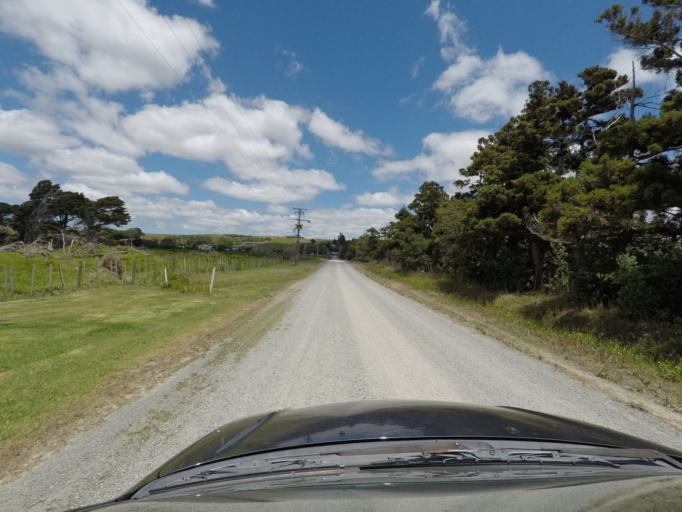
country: NZ
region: Northland
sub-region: Whangarei
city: Ruakaka
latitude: -35.9979
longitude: 174.4790
